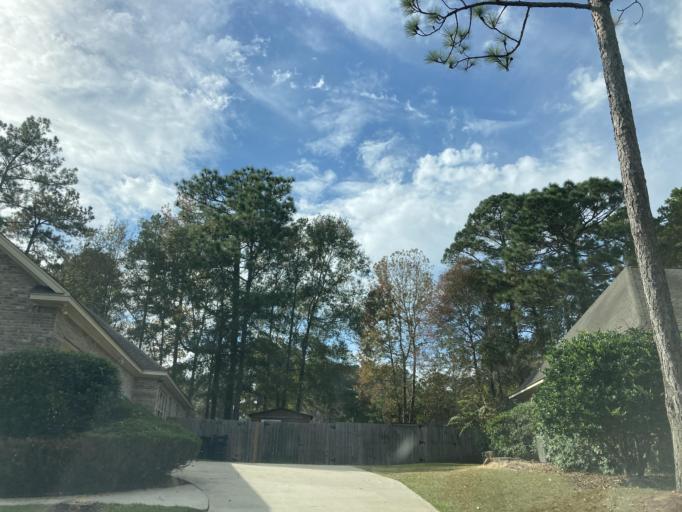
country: US
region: Mississippi
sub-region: Lamar County
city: Arnold Line
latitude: 31.3337
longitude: -89.4368
